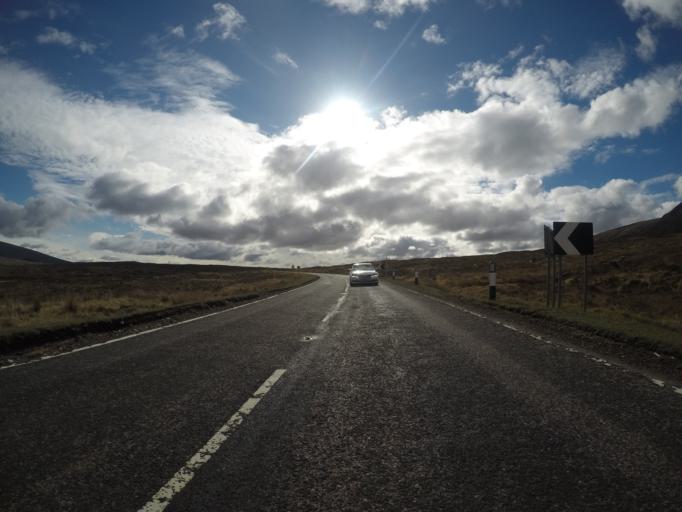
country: GB
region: Scotland
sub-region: Highland
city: Spean Bridge
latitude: 56.6470
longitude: -4.8423
